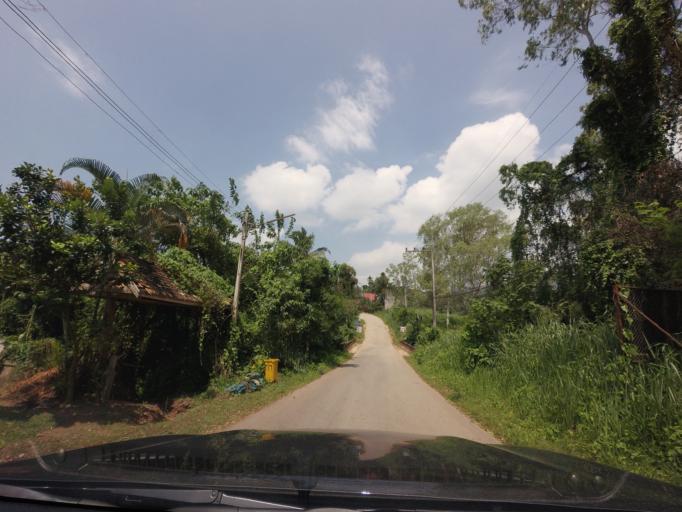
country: TH
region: Loei
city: Phu Ruea
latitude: 17.4570
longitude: 101.3592
